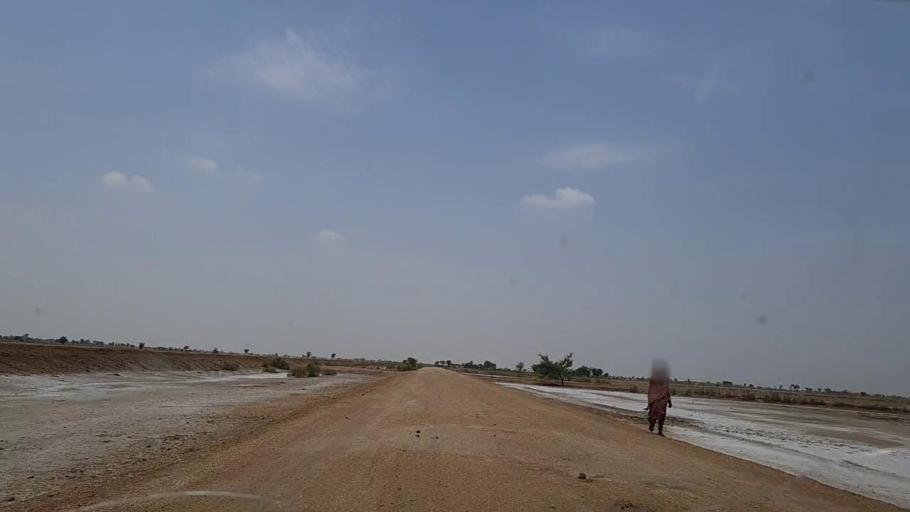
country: PK
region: Sindh
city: Phulji
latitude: 26.7989
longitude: 67.6371
